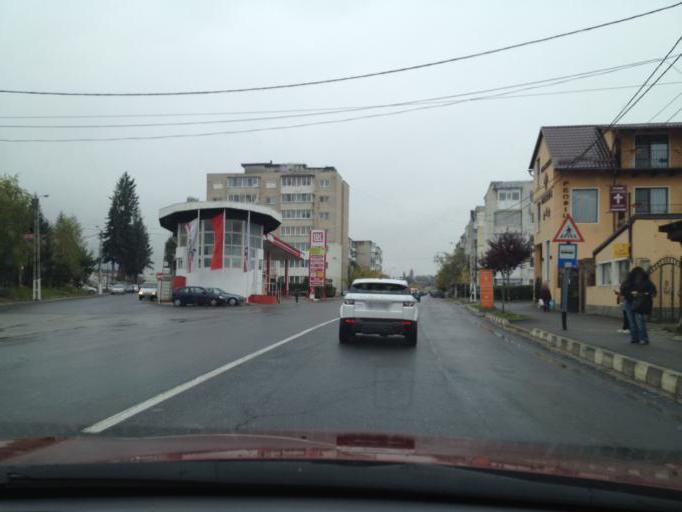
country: RO
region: Brasov
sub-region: Comuna Cristian
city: Cristian
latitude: 45.5994
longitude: 25.4651
